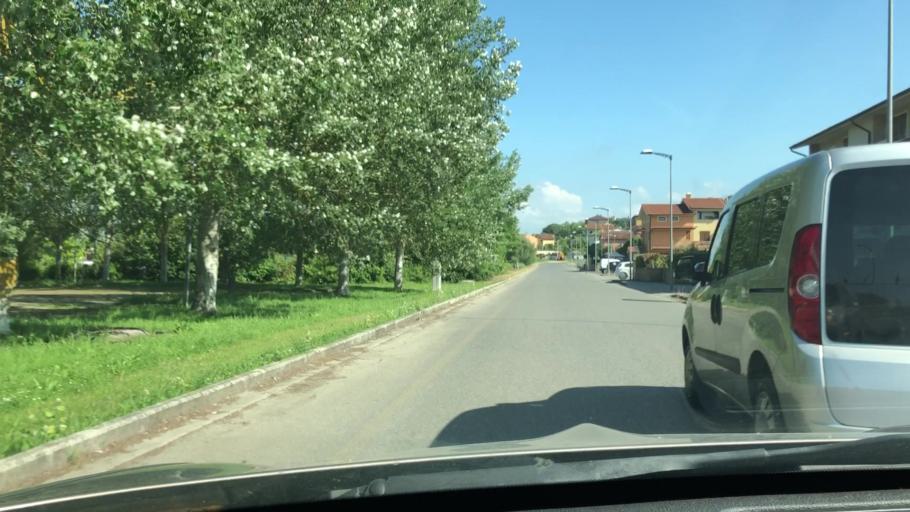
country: IT
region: Tuscany
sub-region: Province of Pisa
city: Capannoli
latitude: 43.5903
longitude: 10.6742
